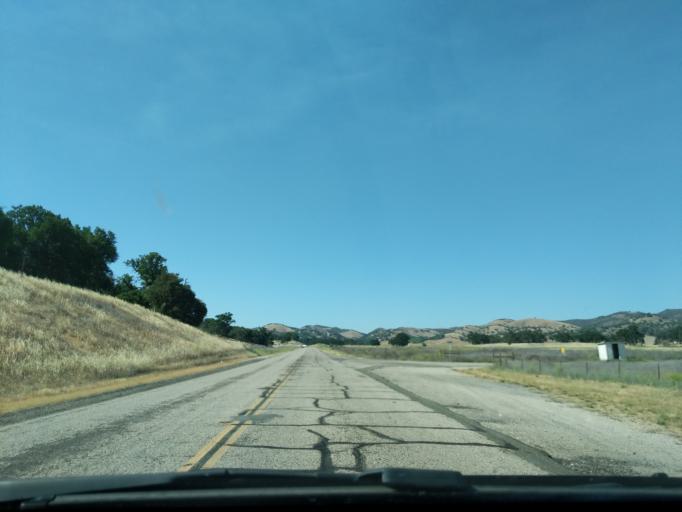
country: US
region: California
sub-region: Monterey County
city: King City
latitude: 36.0246
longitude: -121.1777
